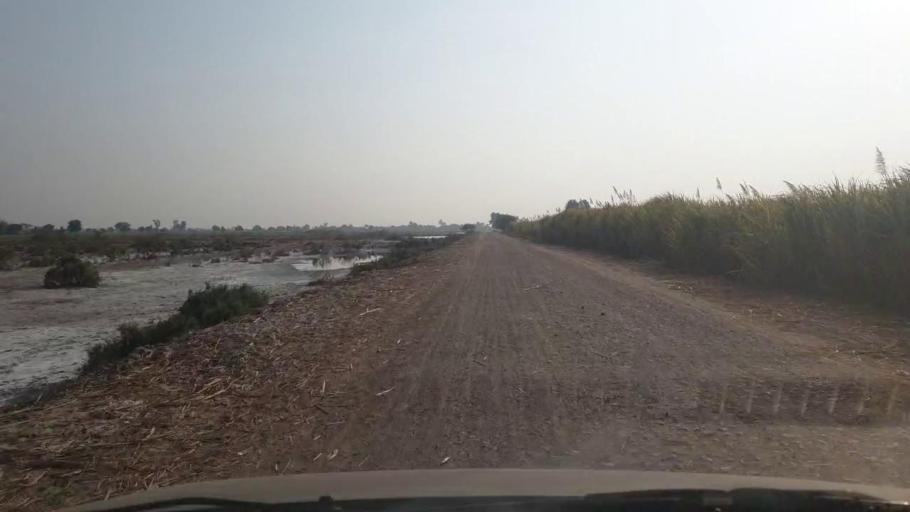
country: PK
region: Sindh
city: Digri
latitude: 25.2603
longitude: 69.1635
